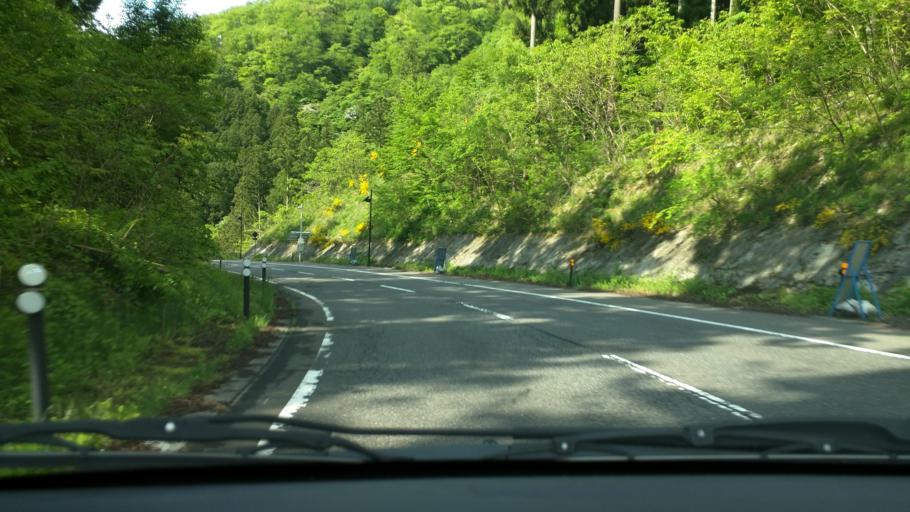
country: JP
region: Tochigi
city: Kuroiso
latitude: 37.2109
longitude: 140.0976
